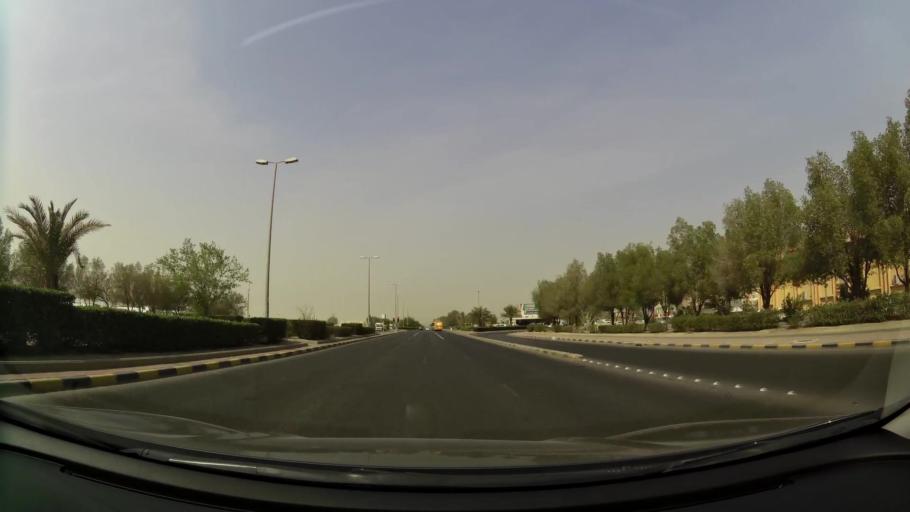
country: KW
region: Al Farwaniyah
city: Al Farwaniyah
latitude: 29.2526
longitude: 47.9230
